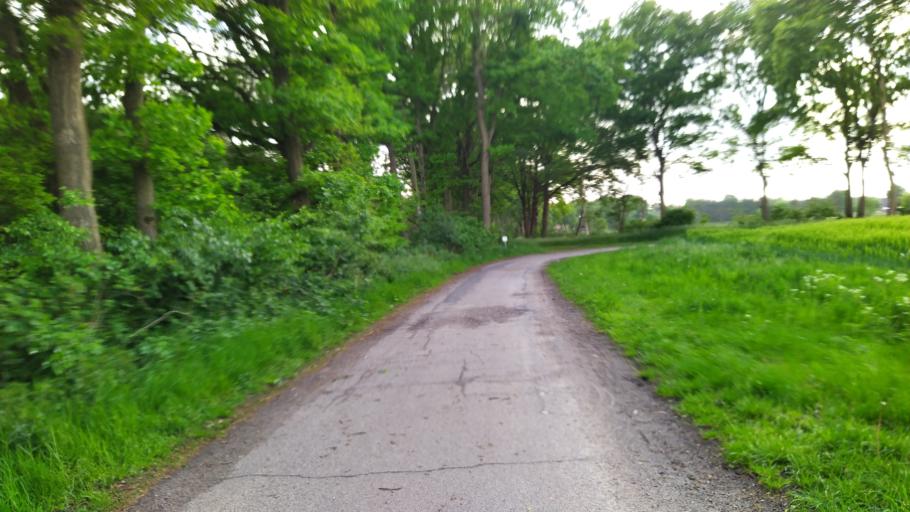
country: DE
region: Lower Saxony
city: Kutenholz
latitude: 53.4699
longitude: 9.3188
